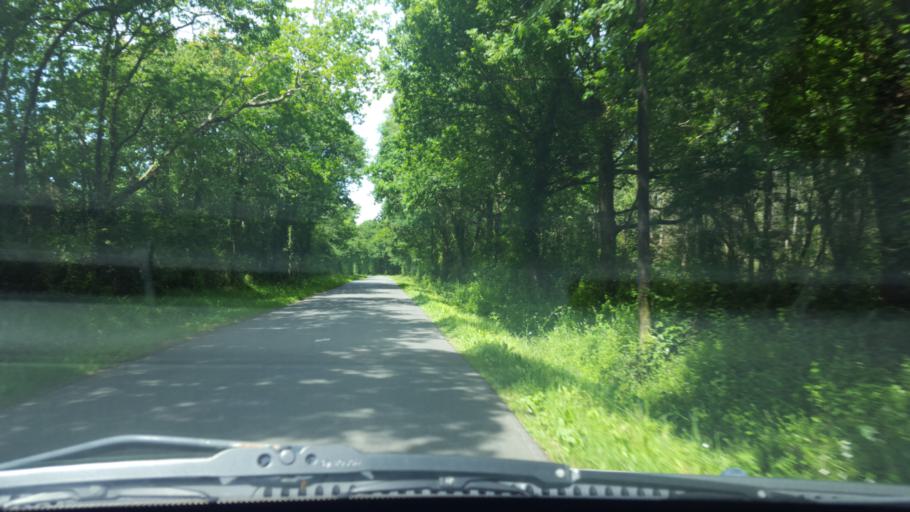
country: FR
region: Pays de la Loire
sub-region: Departement de la Loire-Atlantique
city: La Limouziniere
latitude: 47.0182
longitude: -1.5836
